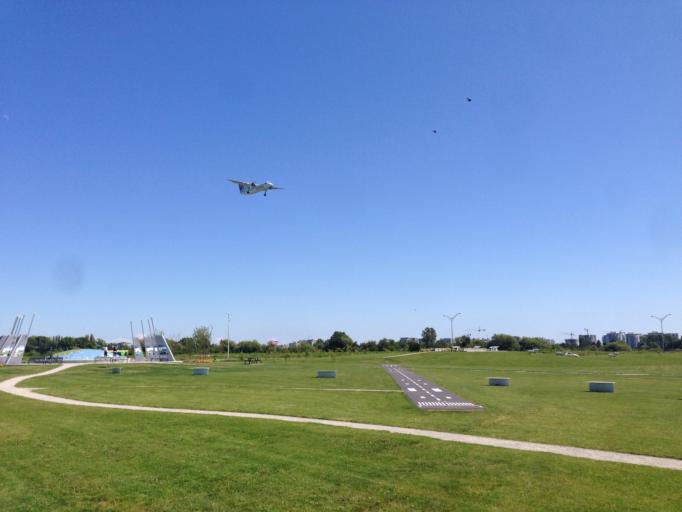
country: CA
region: British Columbia
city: Richmond
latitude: 49.1847
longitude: -123.1499
